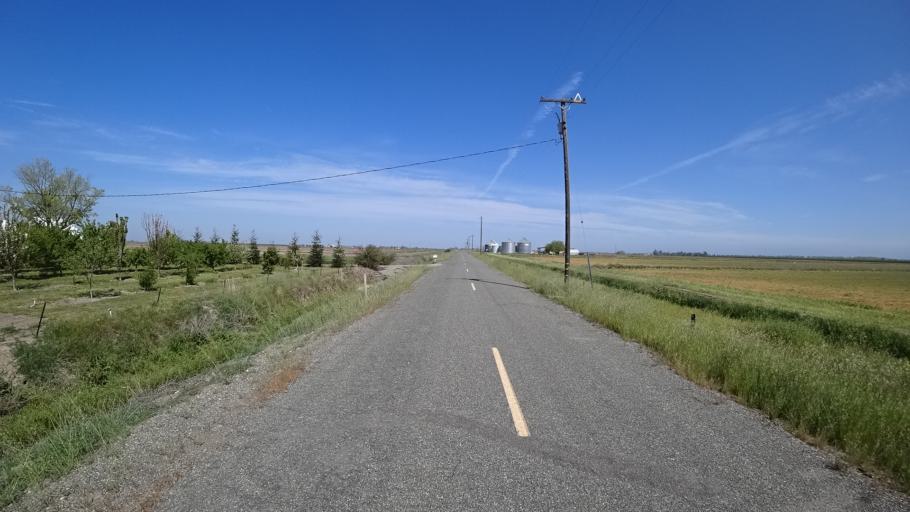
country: US
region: California
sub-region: Glenn County
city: Hamilton City
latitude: 39.5910
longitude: -122.0276
